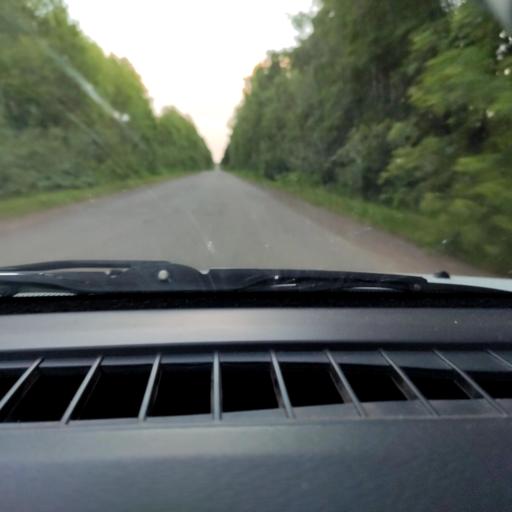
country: RU
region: Perm
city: Orda
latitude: 57.2649
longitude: 56.5339
